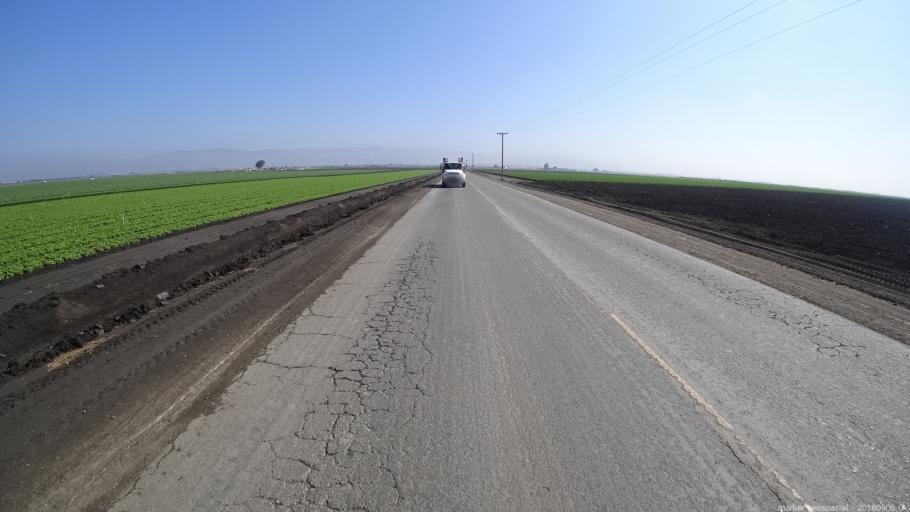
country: US
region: California
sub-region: Monterey County
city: Chualar
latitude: 36.5563
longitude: -121.5337
